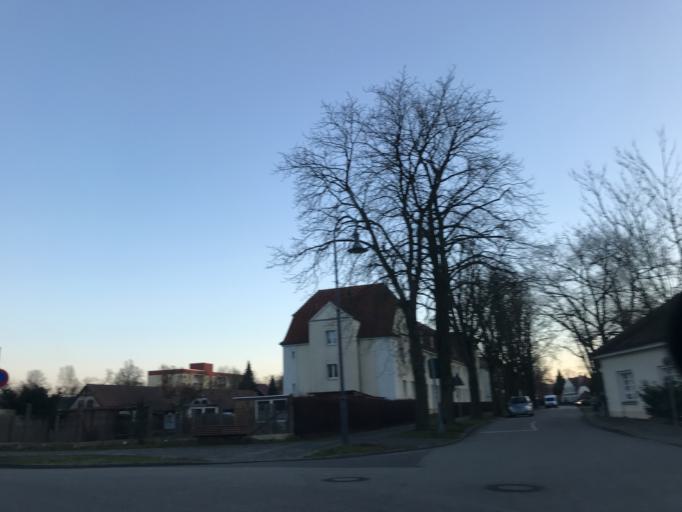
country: DE
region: Brandenburg
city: Premnitz
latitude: 52.5338
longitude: 12.3400
